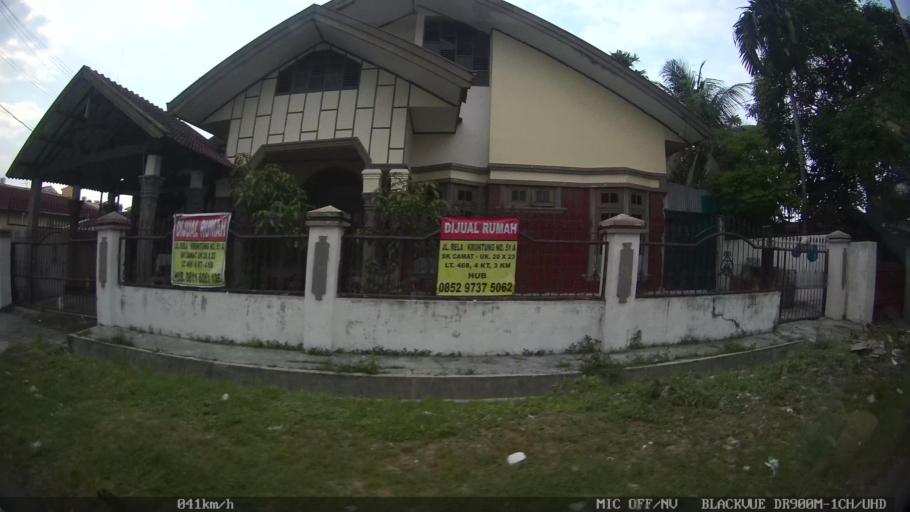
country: ID
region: North Sumatra
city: Medan
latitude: 3.6072
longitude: 98.6990
